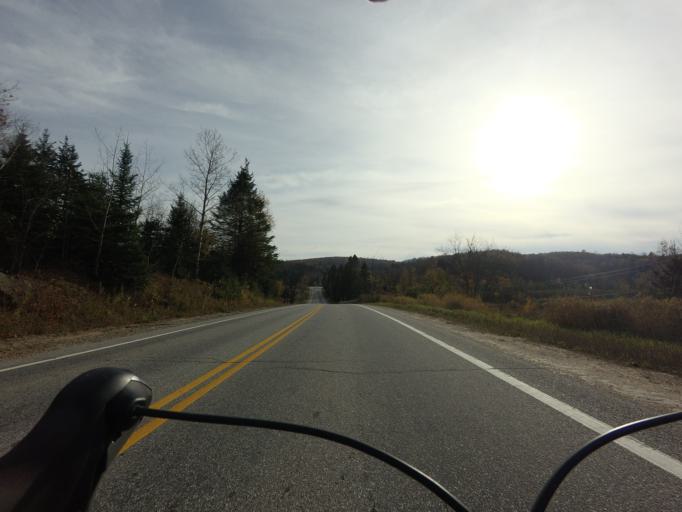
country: CA
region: Quebec
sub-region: Outaouais
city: Val-des-Monts
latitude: 45.6677
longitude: -75.7347
